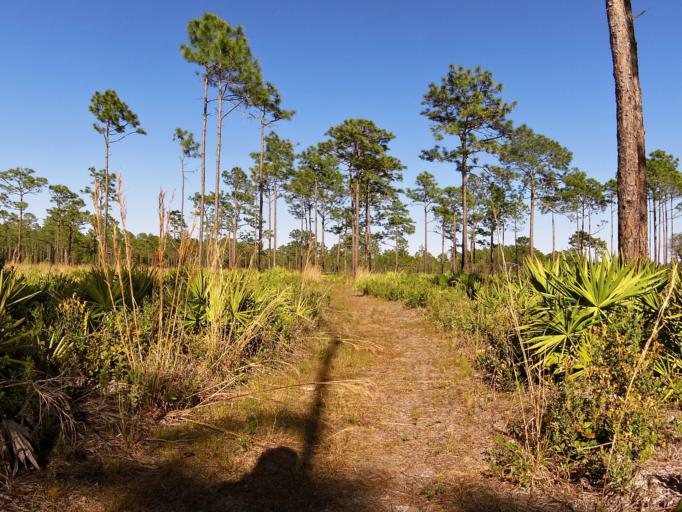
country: US
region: Florida
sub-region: Duval County
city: Atlantic Beach
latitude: 30.4749
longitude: -81.4976
